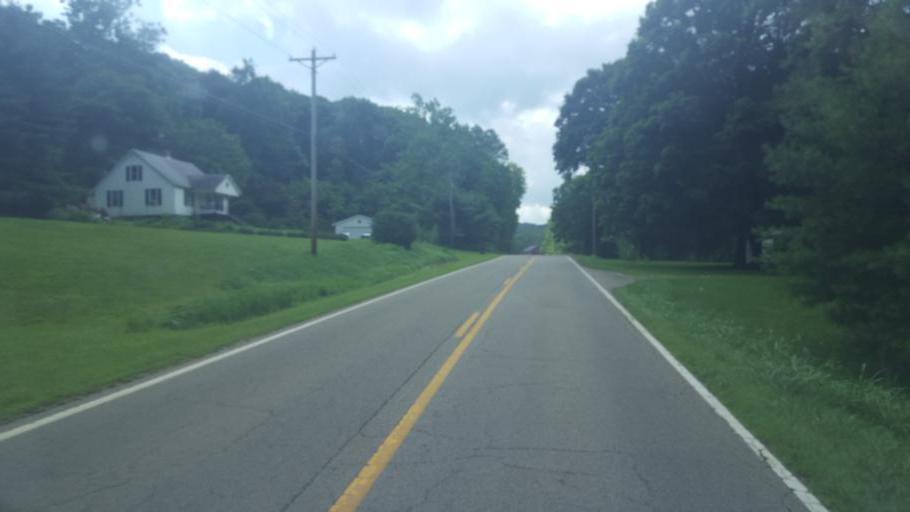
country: US
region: Ohio
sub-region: Ross County
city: Kingston
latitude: 39.4502
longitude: -82.7510
